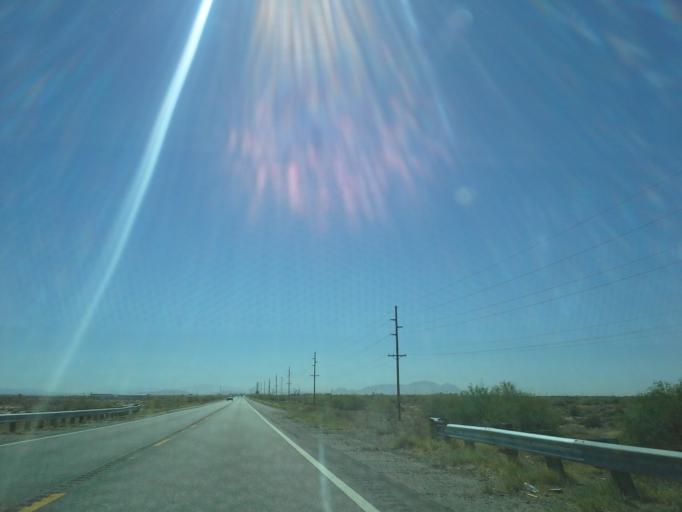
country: US
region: Arizona
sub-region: Pinal County
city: Blackwater
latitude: 33.0127
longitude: -111.6245
